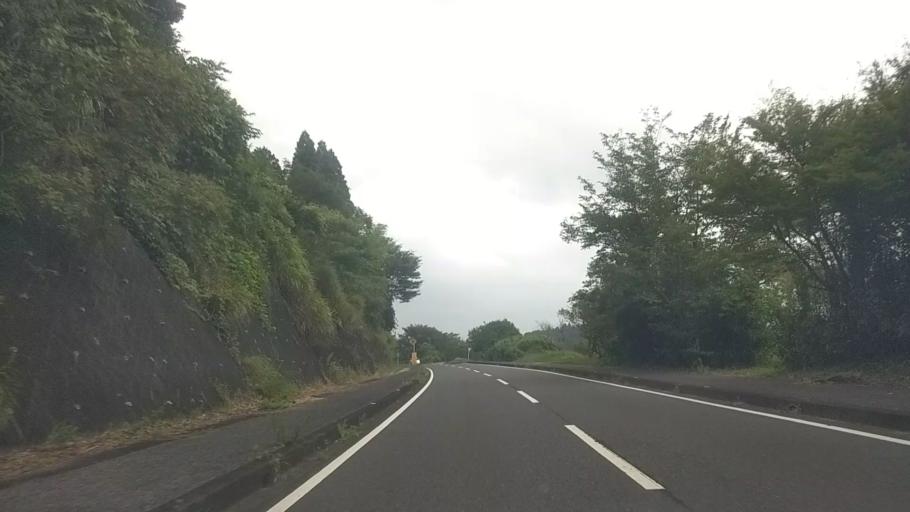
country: JP
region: Chiba
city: Kawaguchi
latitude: 35.2414
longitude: 140.0834
